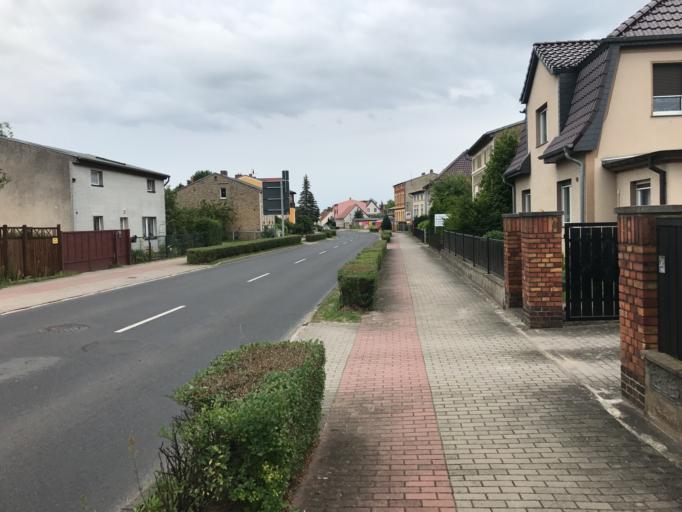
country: DE
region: Brandenburg
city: Marienwerder
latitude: 52.8506
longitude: 13.6755
